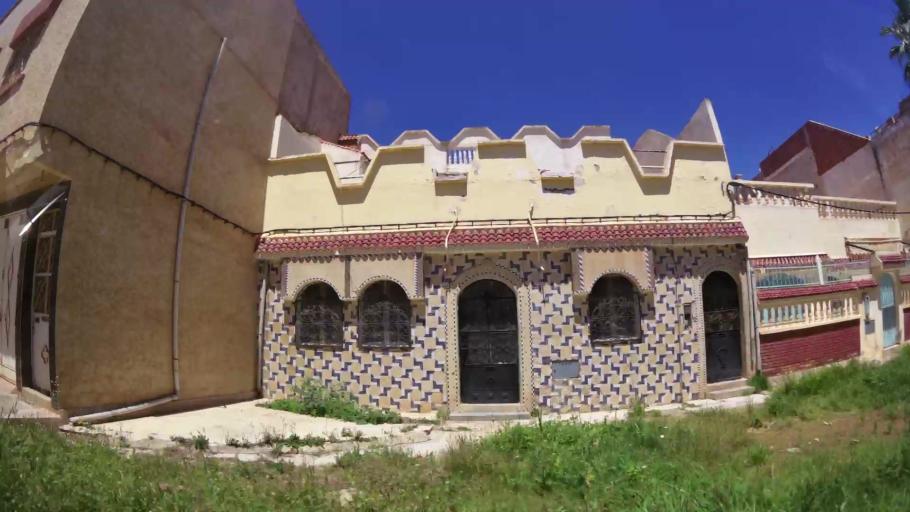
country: MA
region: Oriental
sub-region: Berkane-Taourirt
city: Madagh
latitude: 35.0800
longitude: -2.2190
